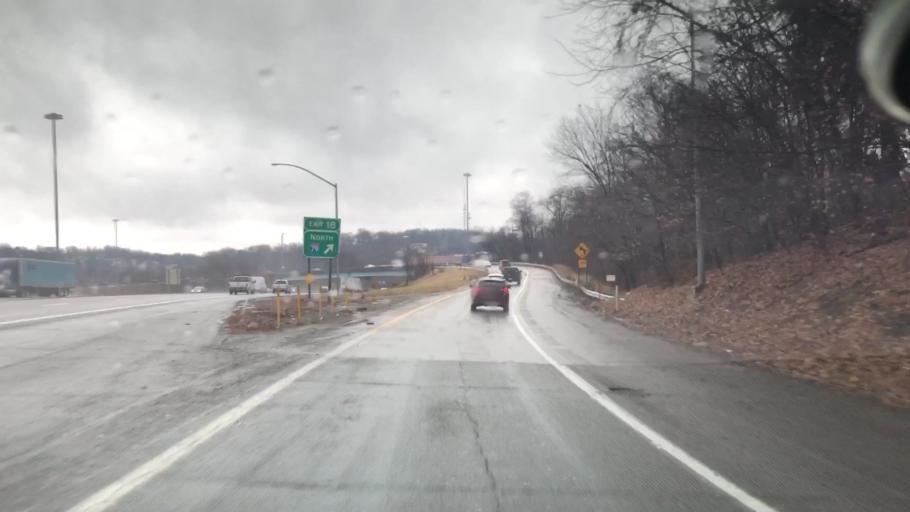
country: US
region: Pennsylvania
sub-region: Washington County
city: Washington
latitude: 40.1877
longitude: -80.2492
